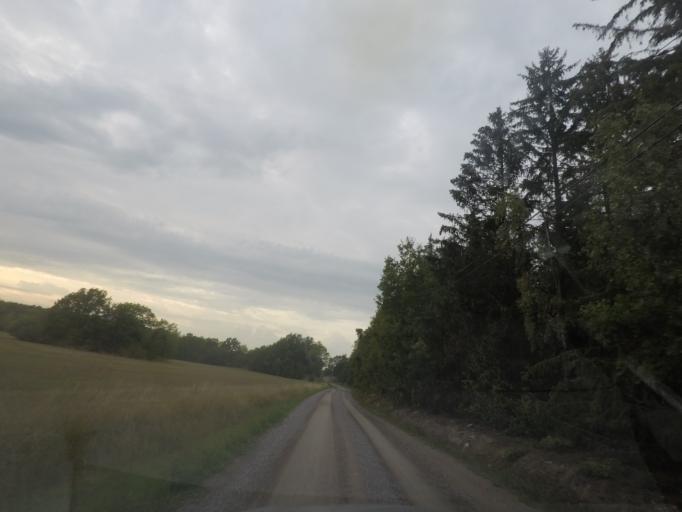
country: SE
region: Vaestmanland
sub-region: Hallstahammars Kommun
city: Kolback
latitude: 59.4812
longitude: 16.1914
